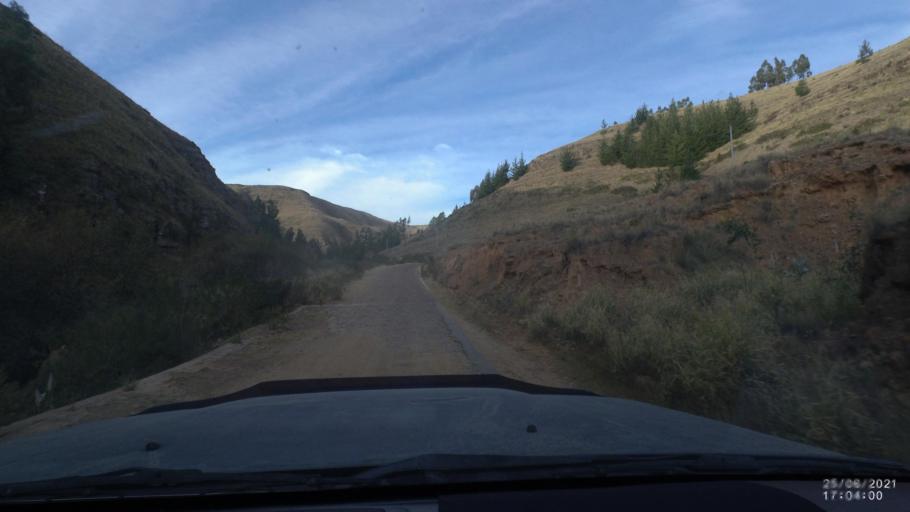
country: BO
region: Cochabamba
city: Arani
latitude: -17.8328
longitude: -65.7244
